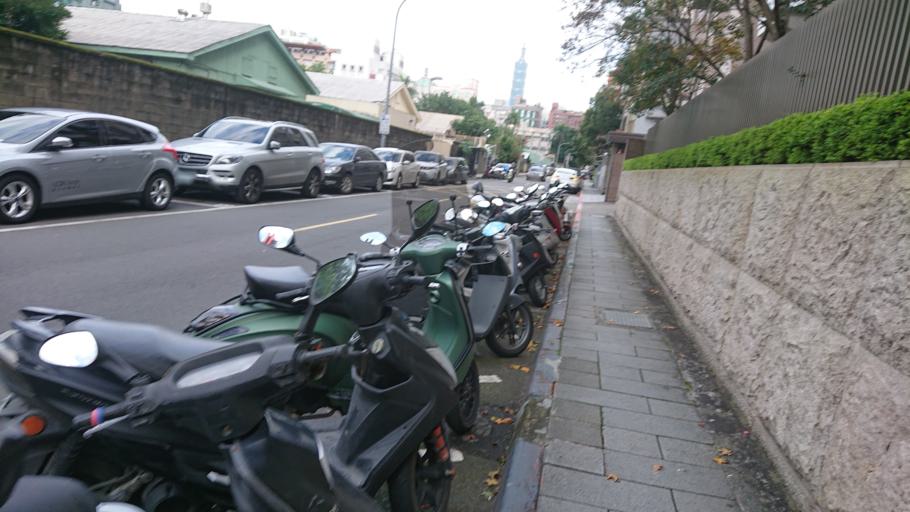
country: TW
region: Taipei
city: Taipei
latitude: 25.0311
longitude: 121.5397
